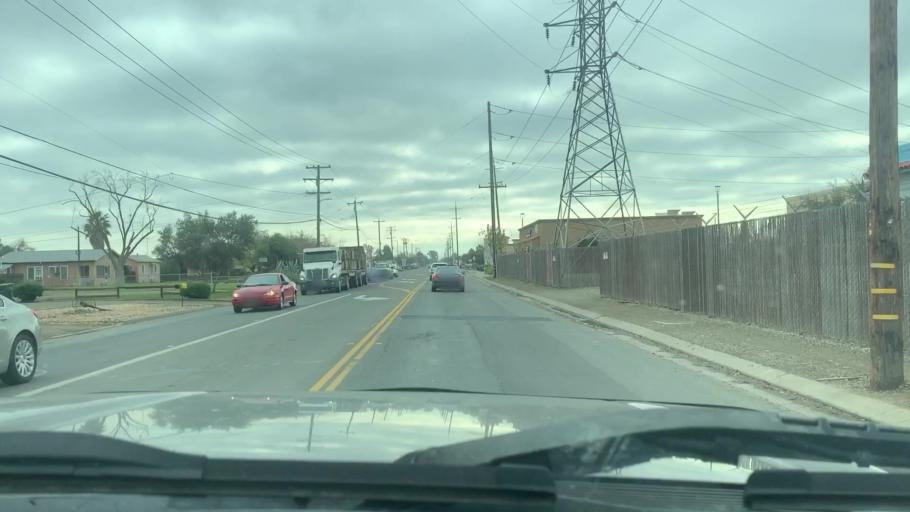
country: US
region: California
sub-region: Merced County
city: Los Banos
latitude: 37.0667
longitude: -120.8353
